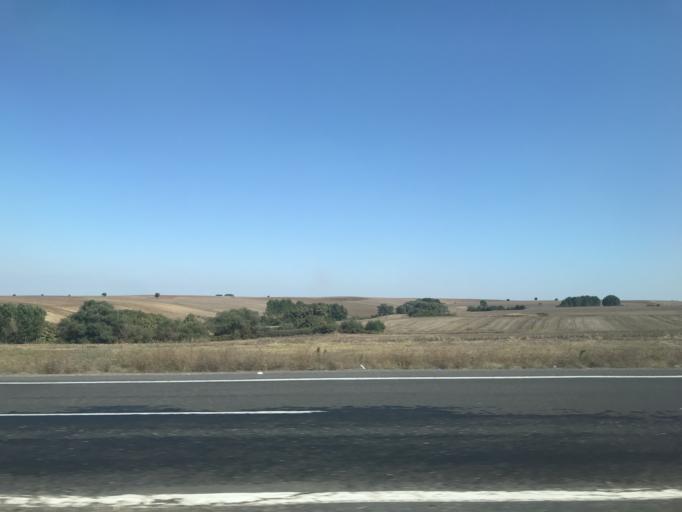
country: TR
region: Tekirdag
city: Muratli
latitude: 41.1163
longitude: 27.4904
